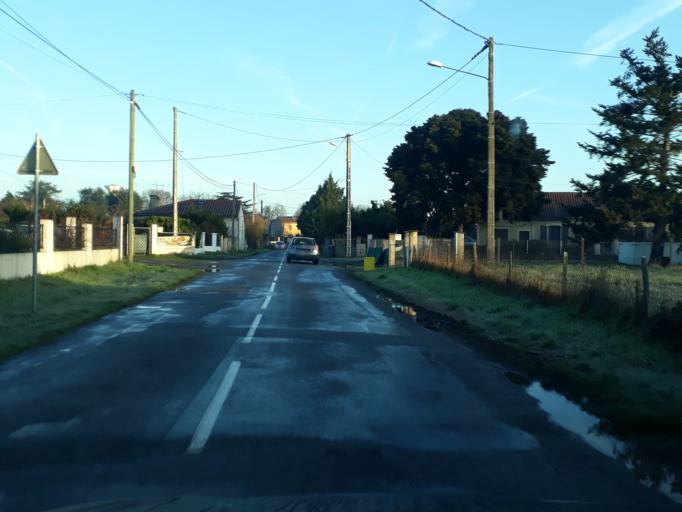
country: FR
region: Midi-Pyrenees
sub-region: Departement de la Haute-Garonne
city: Longages
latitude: 43.3511
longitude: 1.2369
